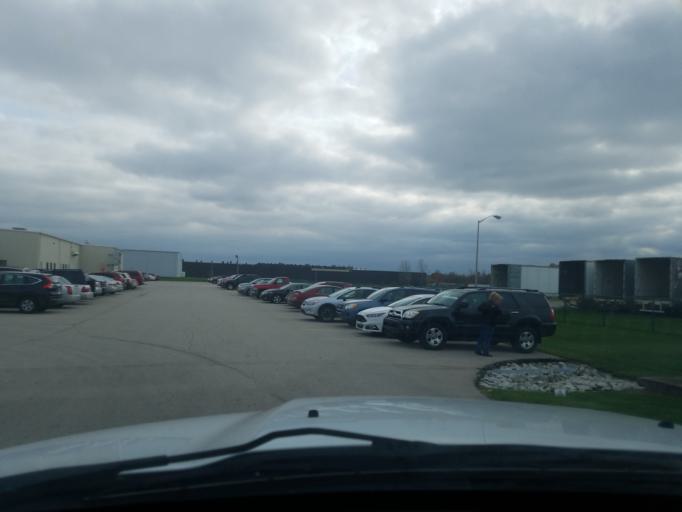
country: US
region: Indiana
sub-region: Shelby County
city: Shelbyville
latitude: 39.5456
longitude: -85.7898
